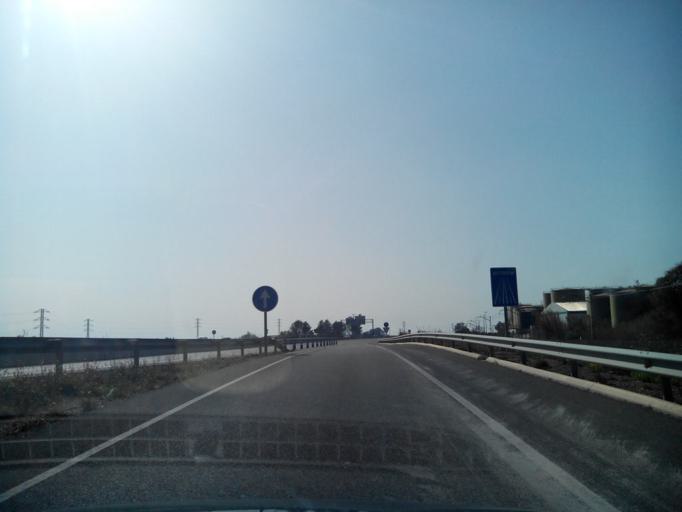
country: ES
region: Catalonia
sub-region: Provincia de Tarragona
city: Alcover
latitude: 41.2521
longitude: 1.1726
